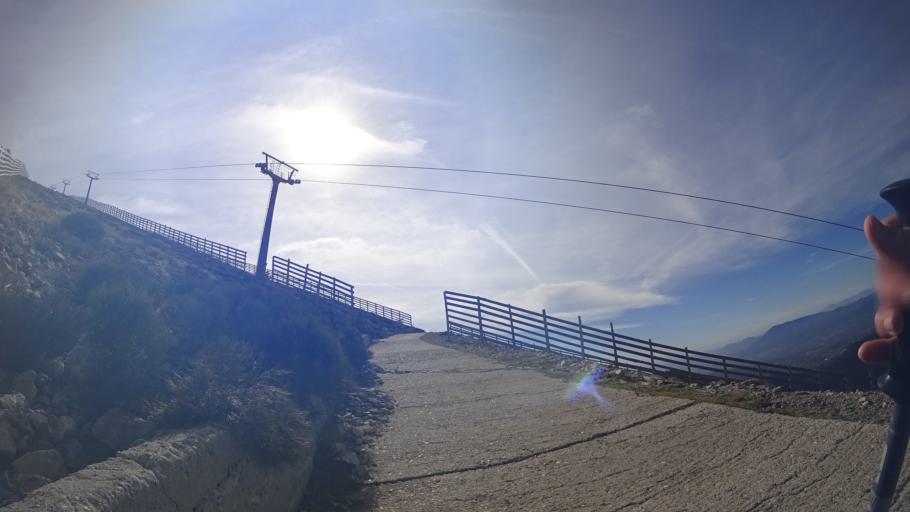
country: ES
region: Madrid
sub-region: Provincia de Madrid
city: Navacerrada
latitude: 40.7867
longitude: -3.9951
